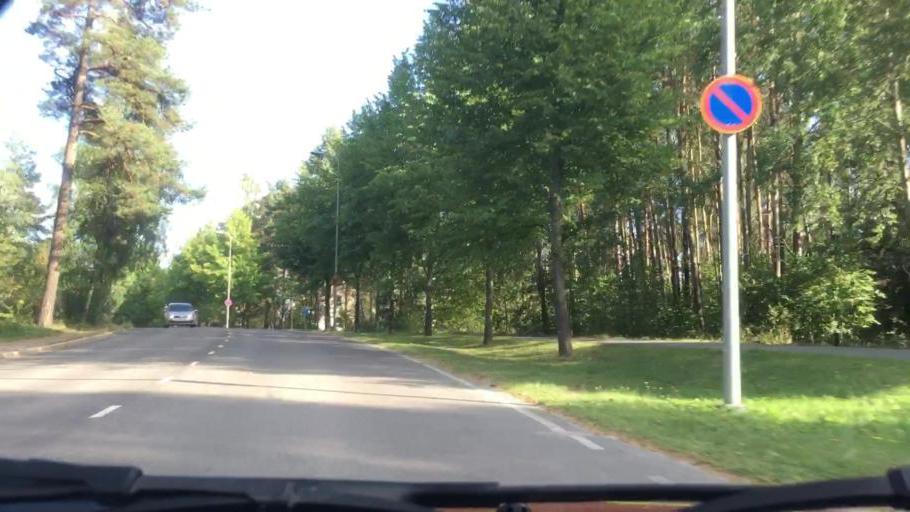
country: FI
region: Varsinais-Suomi
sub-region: Turku
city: Turku
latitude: 60.4651
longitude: 22.2366
